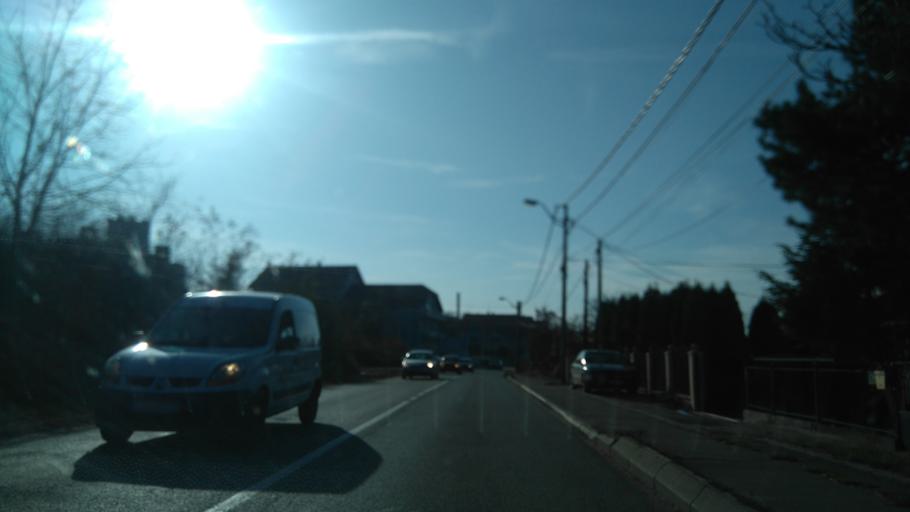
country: RS
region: Central Serbia
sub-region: Belgrade
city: Rakovica
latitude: 44.7371
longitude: 20.3847
